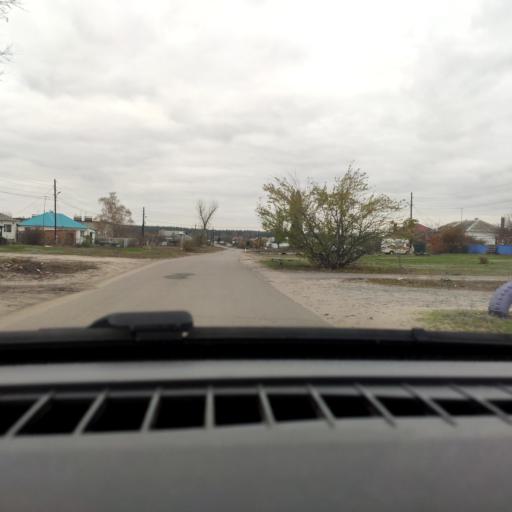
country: RU
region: Voronezj
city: Maslovka
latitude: 51.5793
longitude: 39.3031
